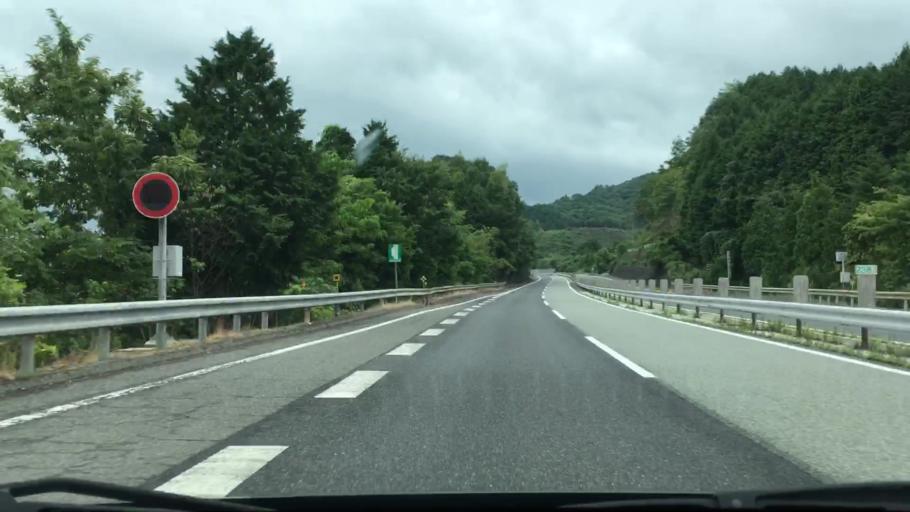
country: JP
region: Okayama
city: Niimi
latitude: 34.9446
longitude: 133.3295
